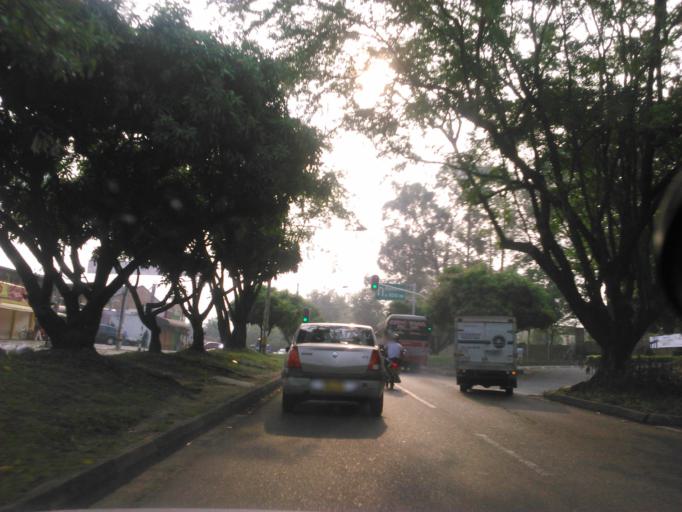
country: CO
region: Antioquia
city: Itagui
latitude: 6.2081
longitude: -75.5915
